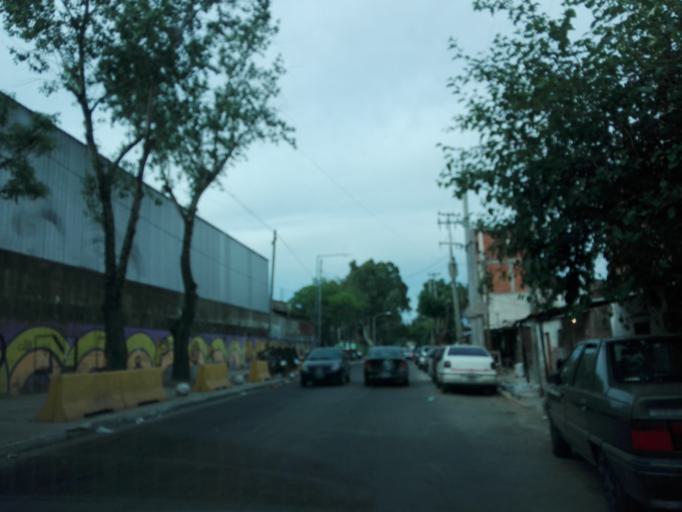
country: AR
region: Buenos Aires
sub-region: Partido de Lanus
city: Lanus
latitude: -34.7012
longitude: -58.3646
